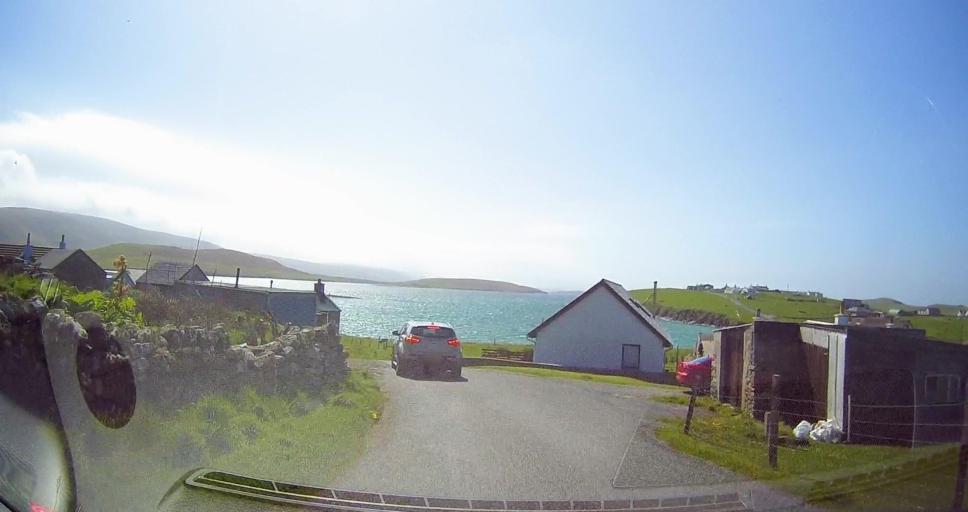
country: GB
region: Scotland
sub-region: Shetland Islands
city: Sandwick
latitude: 60.0662
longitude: -1.3375
